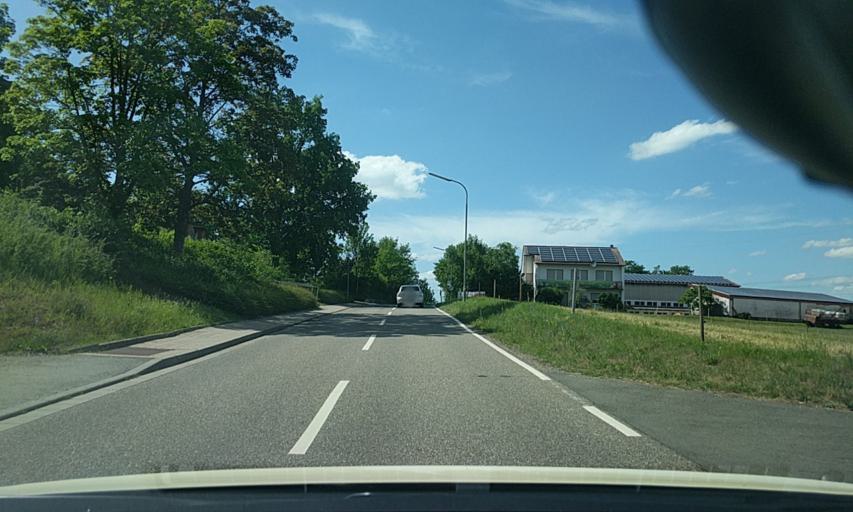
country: DE
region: Rheinland-Pfalz
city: Katzweiler
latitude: 49.4861
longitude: 7.7097
